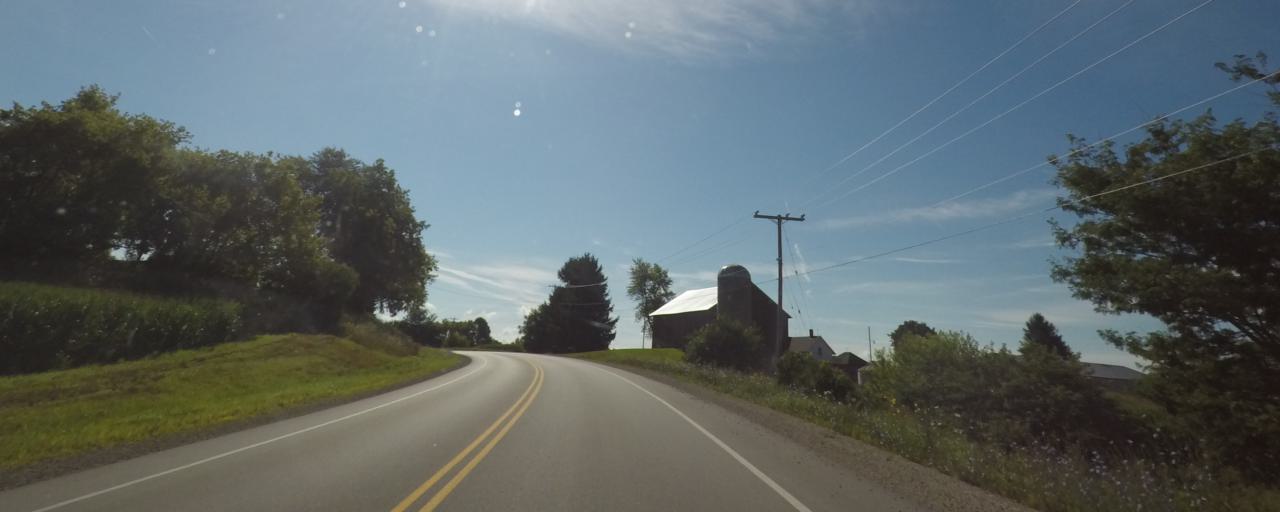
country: US
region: Wisconsin
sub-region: Jefferson County
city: Johnson Creek
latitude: 43.0763
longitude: -88.7453
